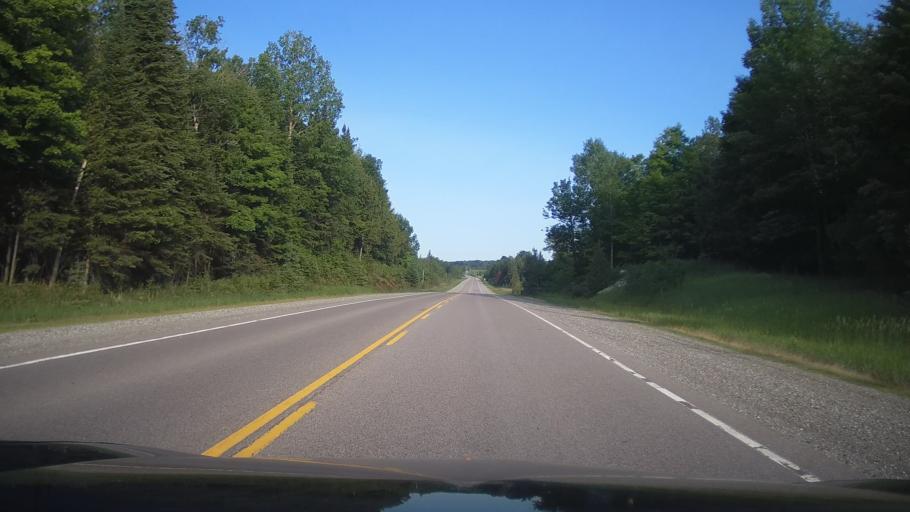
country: CA
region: Ontario
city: Skatepark
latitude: 44.7524
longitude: -76.8403
